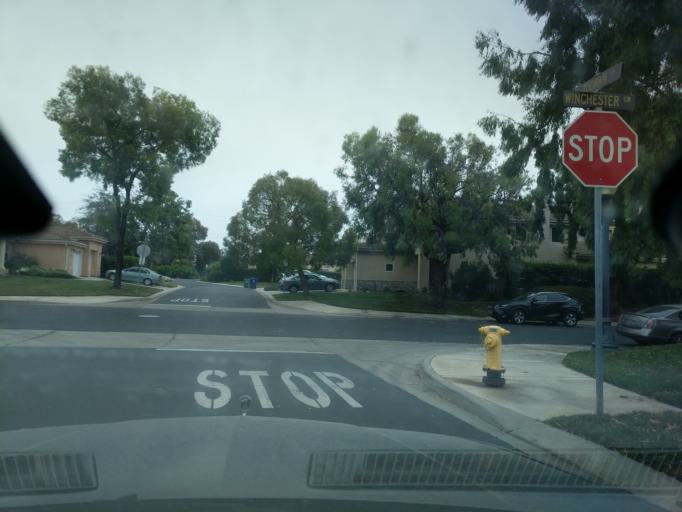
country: US
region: California
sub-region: Santa Barbara County
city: Isla Vista
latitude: 34.4342
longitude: -119.9024
